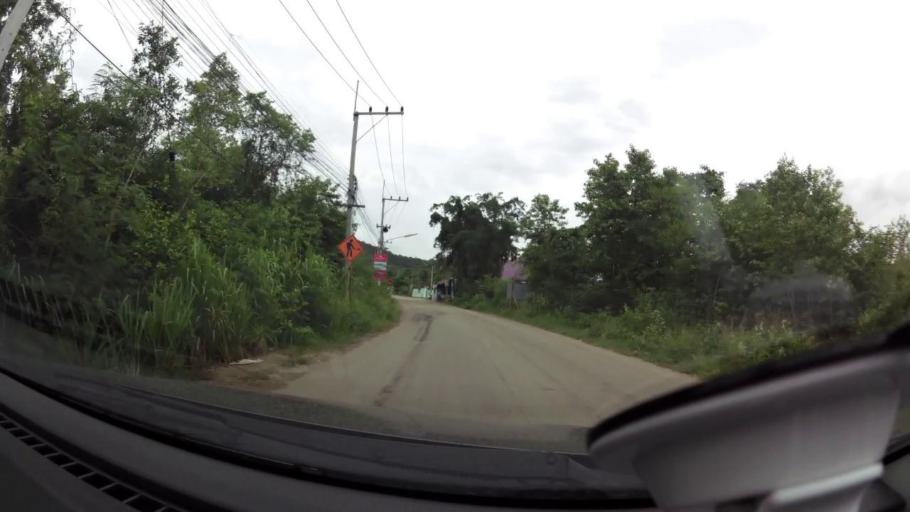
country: TH
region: Prachuap Khiri Khan
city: Pran Buri
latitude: 12.4454
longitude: 99.9703
